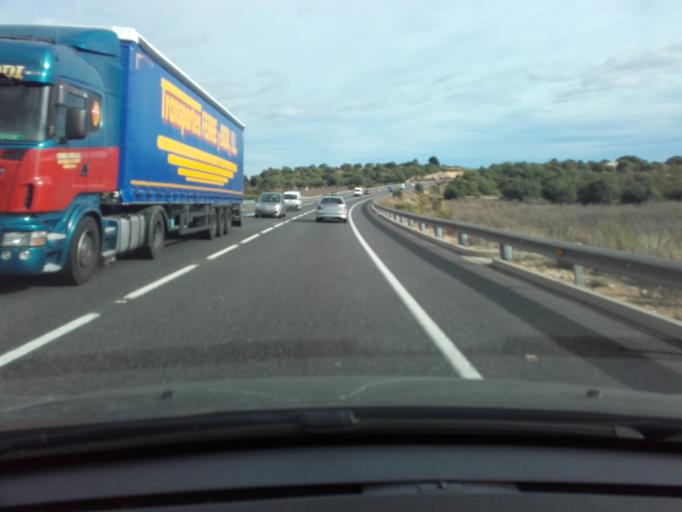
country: ES
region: Catalonia
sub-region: Provincia de Tarragona
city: Torredembarra
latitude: 41.1620
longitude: 1.4050
